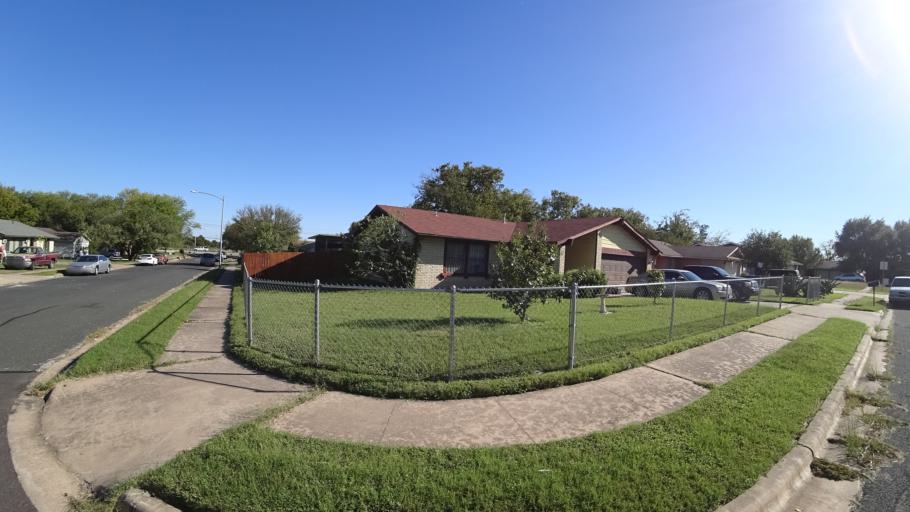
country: US
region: Texas
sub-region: Travis County
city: Hornsby Bend
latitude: 30.2998
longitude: -97.6242
